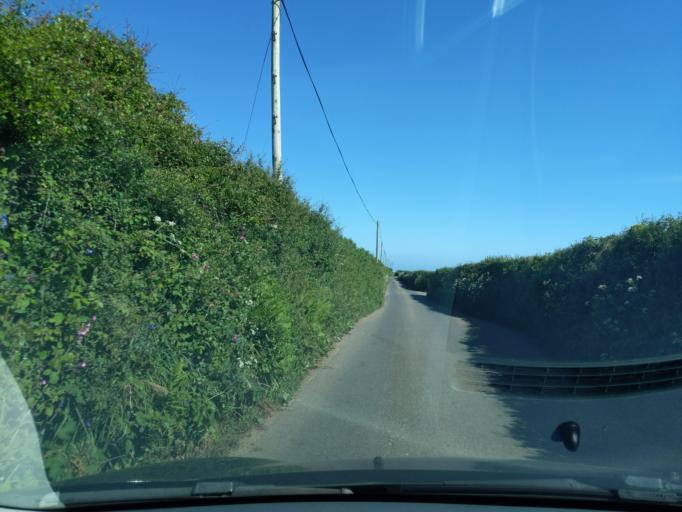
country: GB
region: England
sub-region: Cornwall
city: St. Buryan
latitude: 50.0684
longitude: -5.6079
